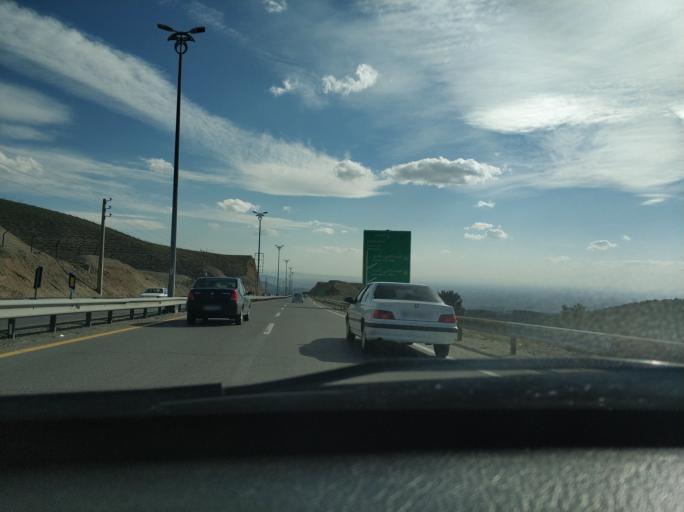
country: IR
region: Tehran
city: Tajrish
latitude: 35.7921
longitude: 51.5692
